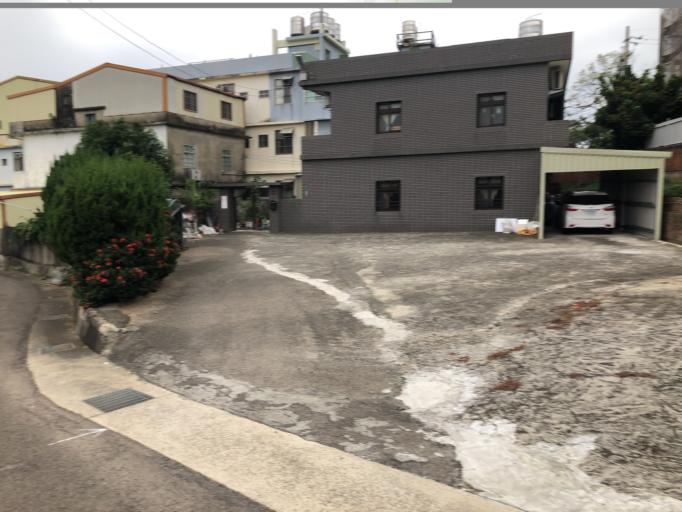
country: TW
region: Taiwan
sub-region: Hsinchu
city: Hsinchu
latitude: 24.7559
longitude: 120.9471
